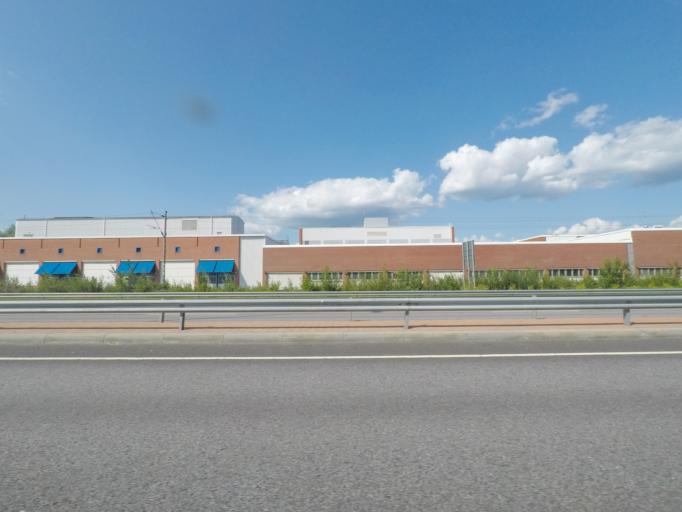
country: FI
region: Southern Savonia
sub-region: Mikkeli
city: Mikkeli
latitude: 61.6778
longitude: 27.2531
